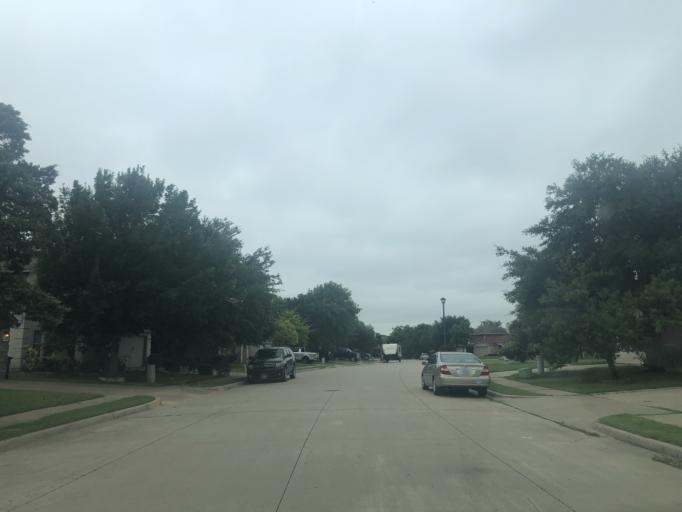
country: US
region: Texas
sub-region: Dallas County
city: Dallas
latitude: 32.7908
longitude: -96.8602
